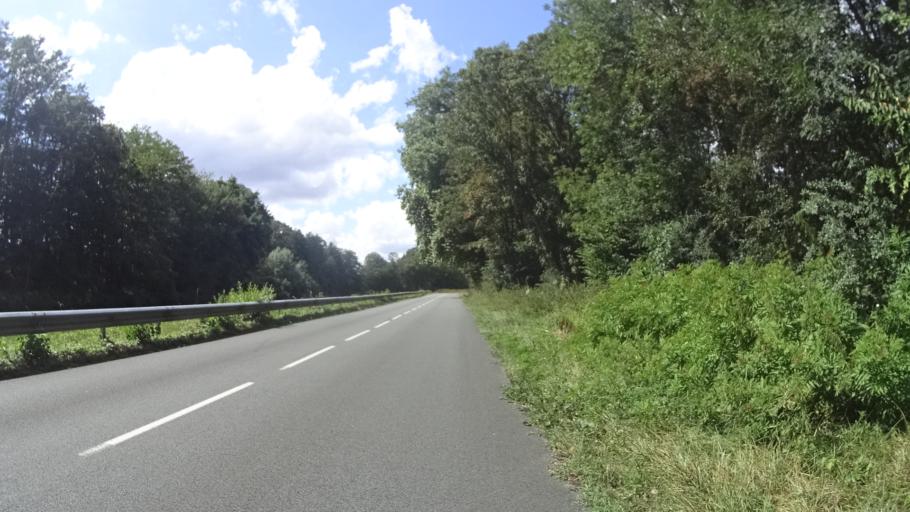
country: FR
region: Bourgogne
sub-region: Departement de Saone-et-Loire
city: Ciry-le-Noble
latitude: 46.5971
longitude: 4.2755
